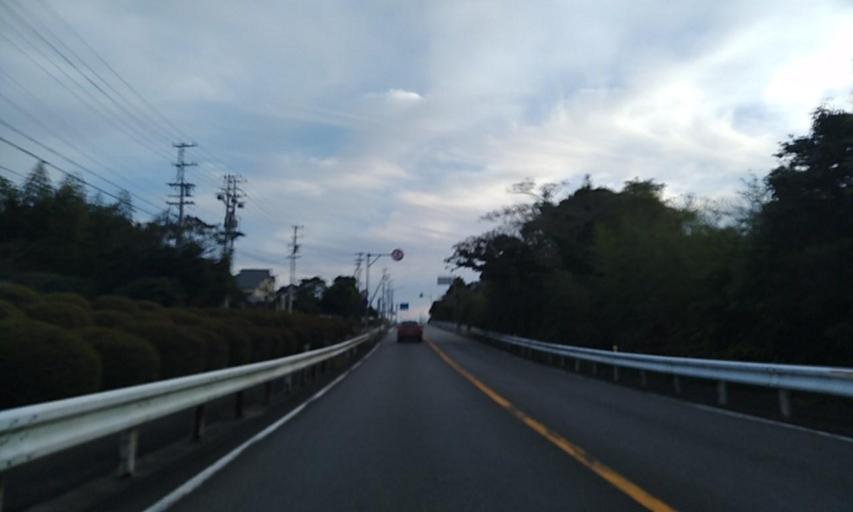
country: JP
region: Mie
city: Toba
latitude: 34.2904
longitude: 136.8829
